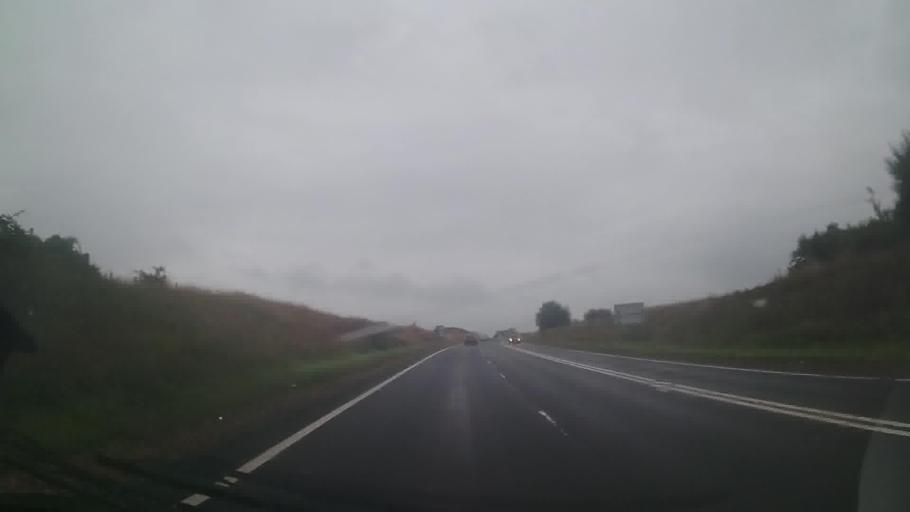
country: GB
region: Scotland
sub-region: North Ayrshire
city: Ardrossan
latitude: 55.6594
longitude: -4.8155
